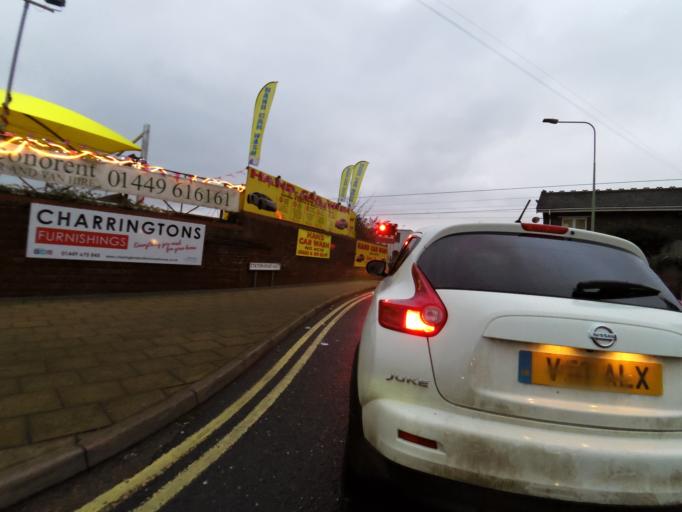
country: GB
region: England
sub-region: Suffolk
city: Stowmarket
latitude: 52.1905
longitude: 0.9991
